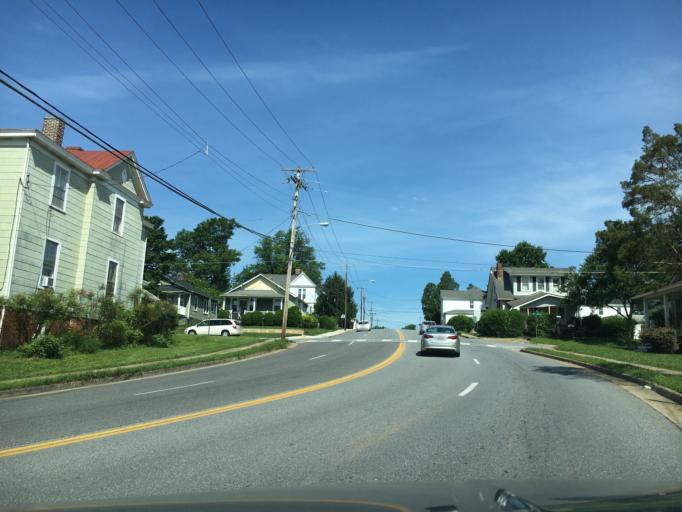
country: US
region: Virginia
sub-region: City of Lynchburg
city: West Lynchburg
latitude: 37.3968
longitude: -79.1676
